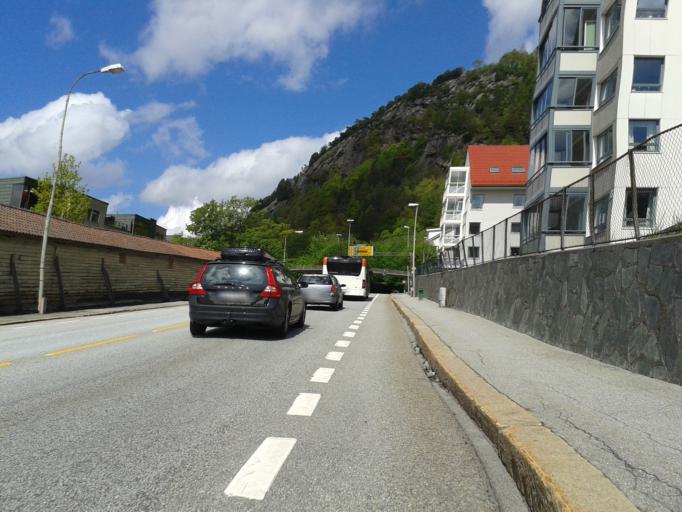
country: NO
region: Hordaland
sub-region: Bergen
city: Bergen
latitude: 60.4129
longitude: 5.3226
